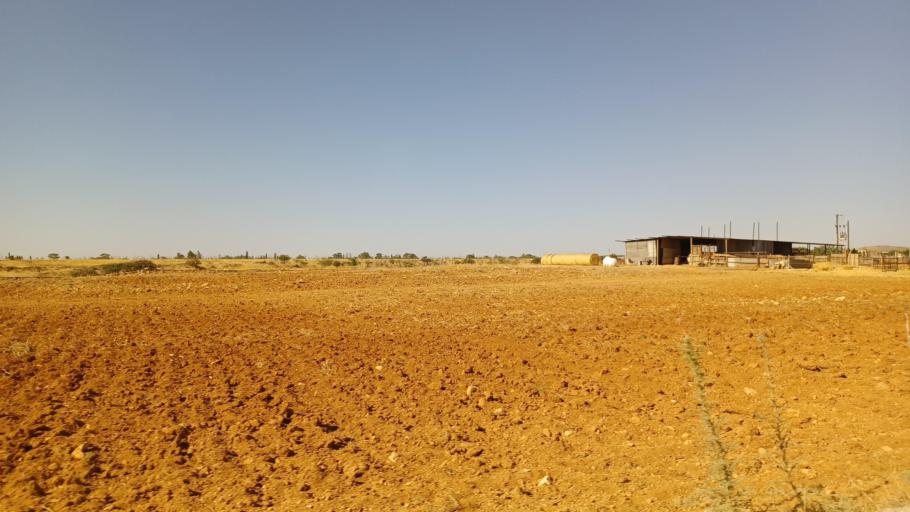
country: CY
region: Larnaka
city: Pergamos
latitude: 35.0528
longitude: 33.6995
